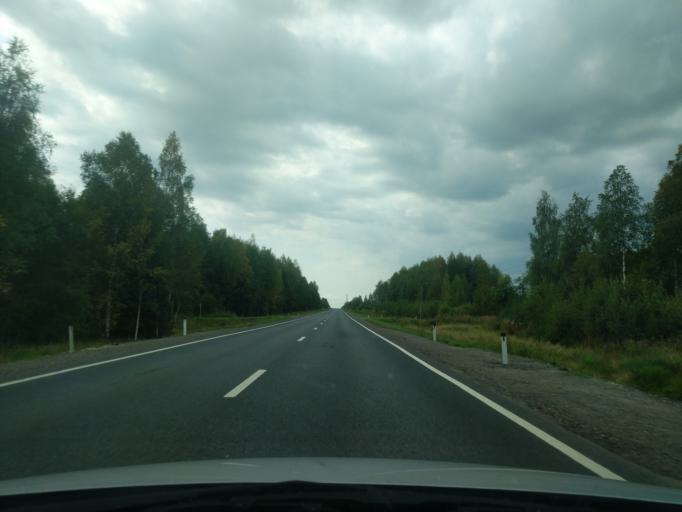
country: RU
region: Kostroma
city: Manturovo
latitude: 58.1513
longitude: 44.3746
